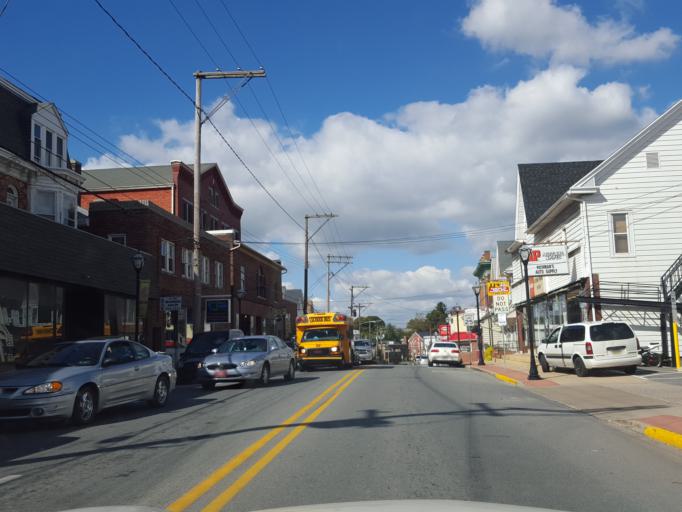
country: US
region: Pennsylvania
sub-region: York County
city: Red Lion
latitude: 39.9012
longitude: -76.6064
